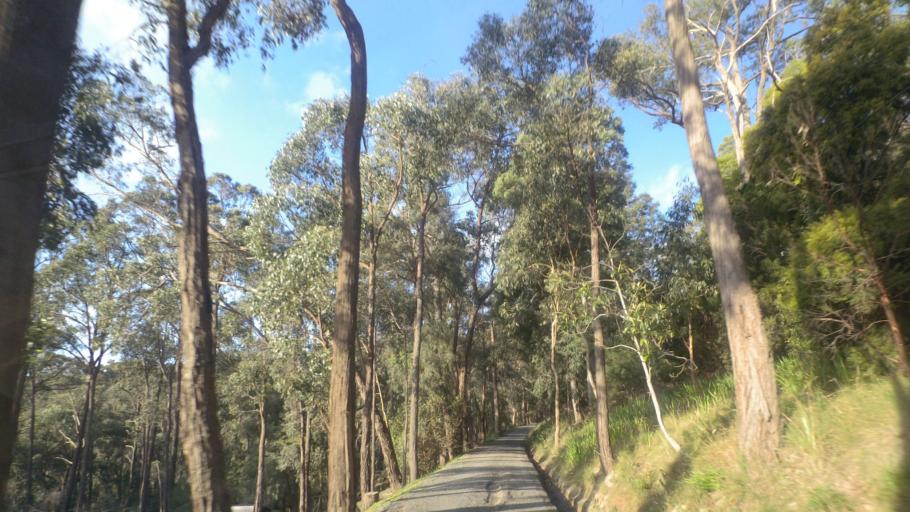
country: AU
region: Victoria
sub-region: Yarra Ranges
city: Kalorama
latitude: -37.8155
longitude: 145.3614
